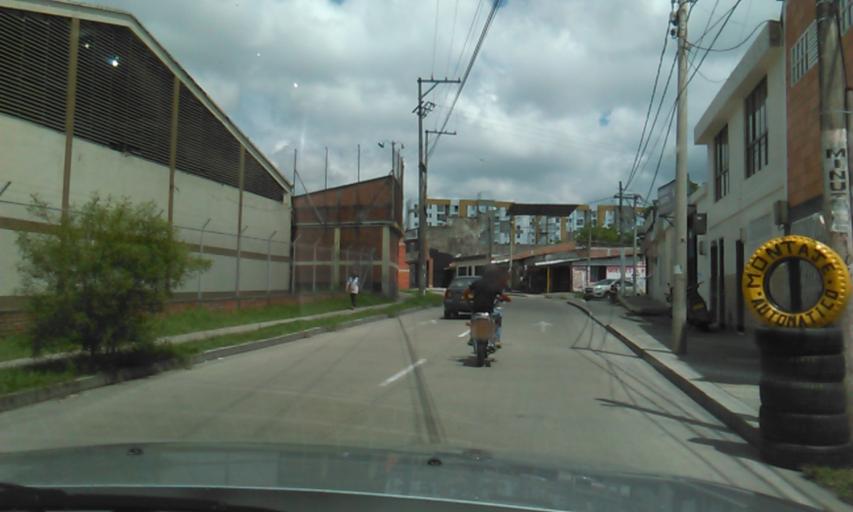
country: CO
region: Quindio
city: Armenia
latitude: 4.5174
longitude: -75.6891
